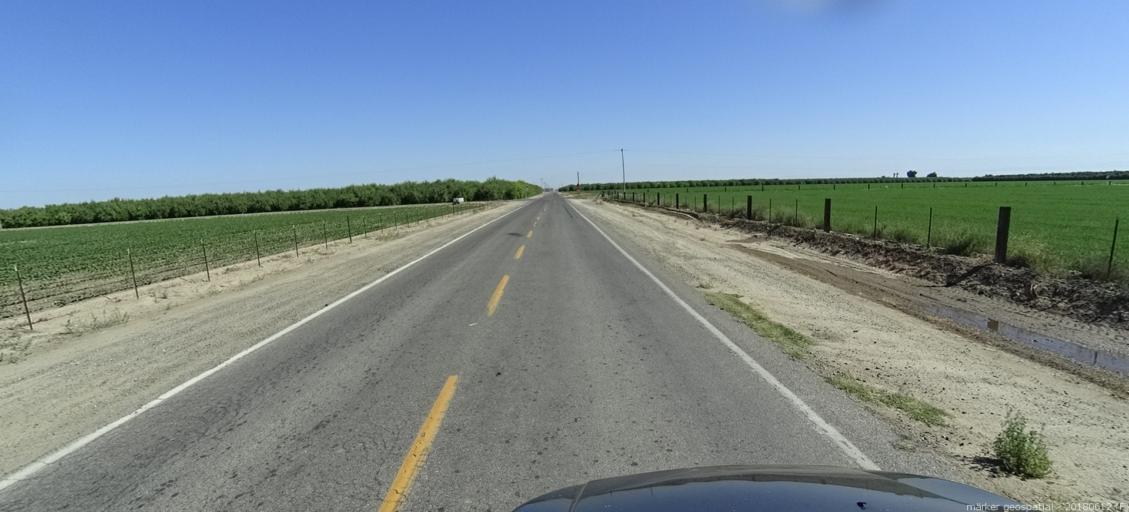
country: US
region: California
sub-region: Madera County
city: Chowchilla
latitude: 37.0168
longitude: -120.3833
